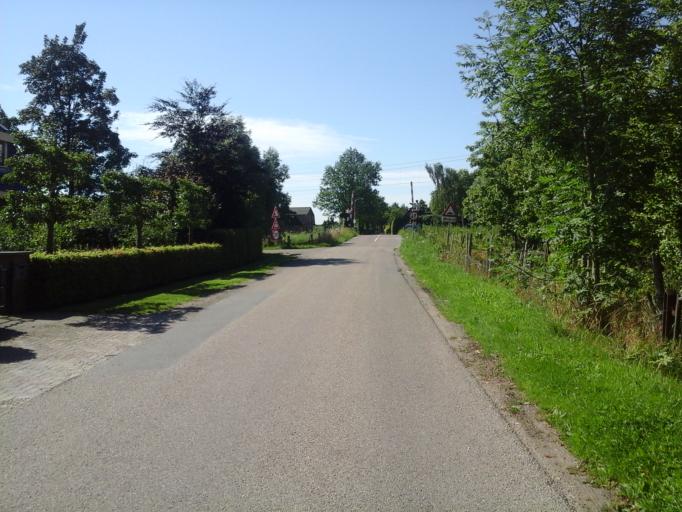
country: NL
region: Gelderland
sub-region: Gemeente Geldermalsen
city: Geldermalsen
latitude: 51.8999
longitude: 5.2604
